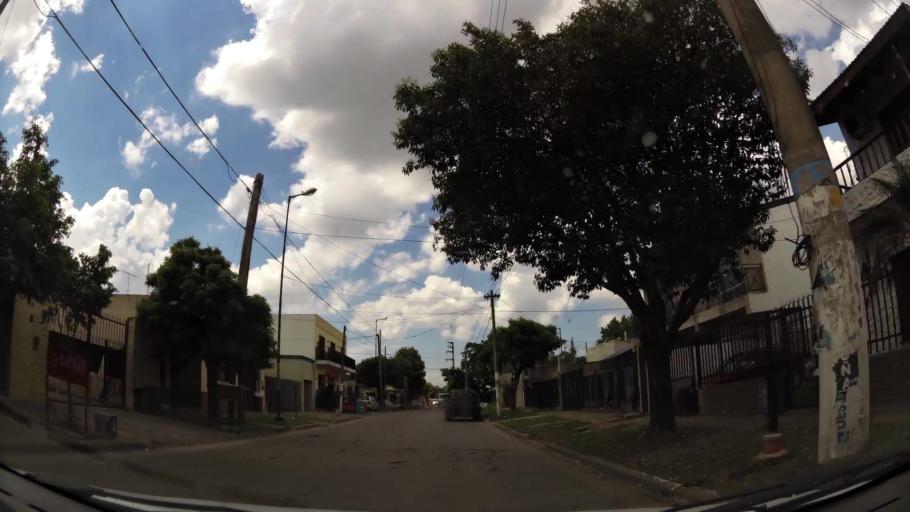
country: AR
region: Buenos Aires
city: Ituzaingo
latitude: -34.6422
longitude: -58.6757
